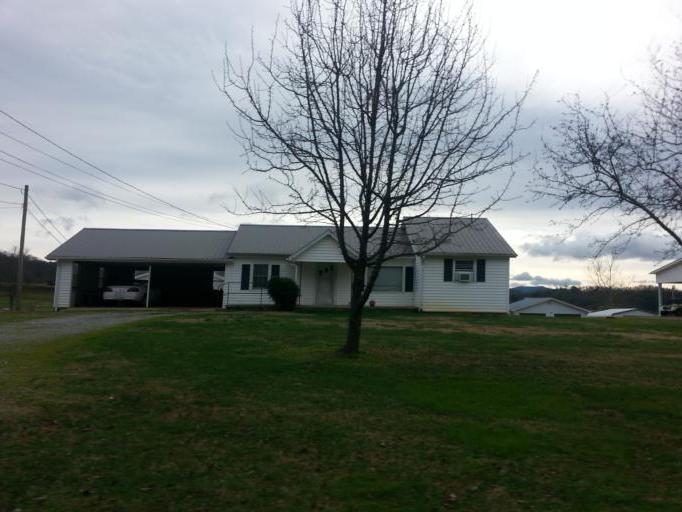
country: US
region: Tennessee
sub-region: Greene County
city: Greeneville
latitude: 36.1332
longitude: -82.8862
